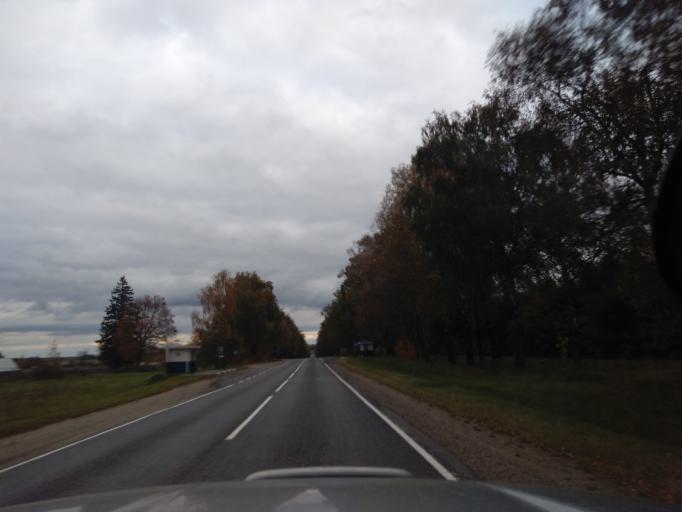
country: BY
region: Minsk
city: Slutsk
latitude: 53.2200
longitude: 27.4655
